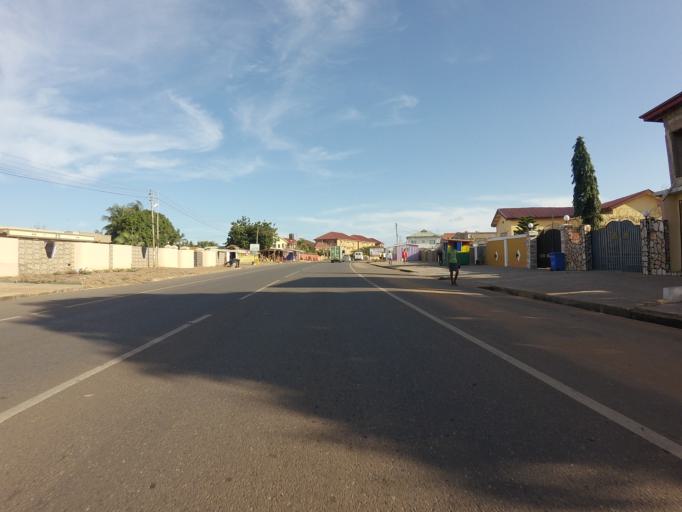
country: GH
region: Greater Accra
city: Nungua
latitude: 5.6343
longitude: -0.0906
